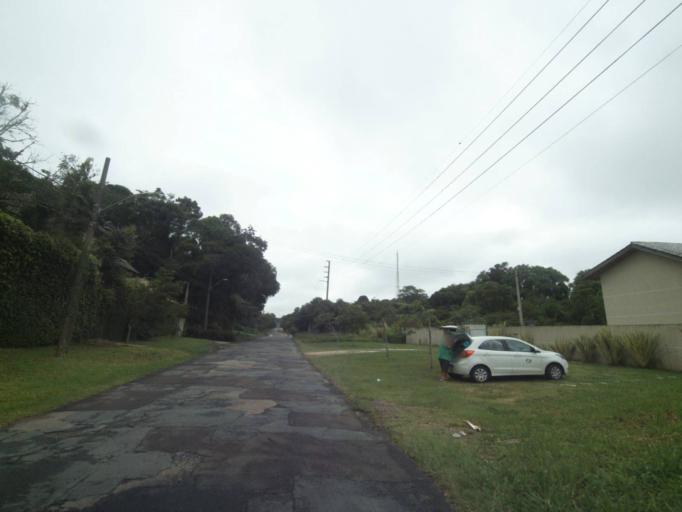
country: BR
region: Parana
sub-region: Curitiba
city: Curitiba
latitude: -25.4144
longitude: -49.2930
